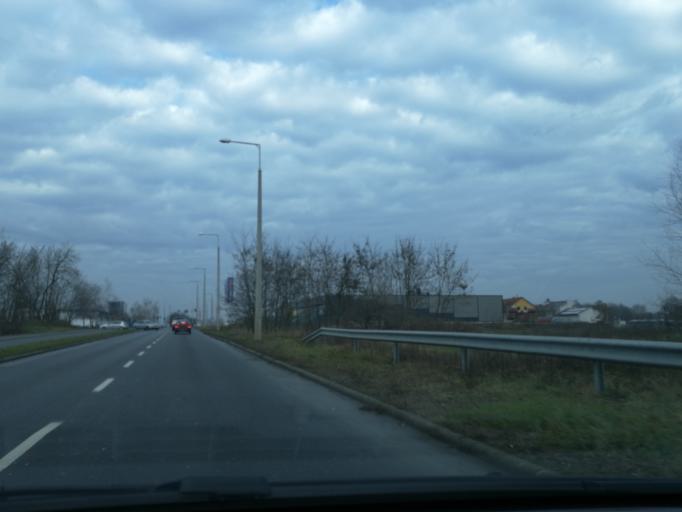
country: HU
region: Szabolcs-Szatmar-Bereg
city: Nyiregyhaza
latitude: 47.9678
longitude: 21.7418
